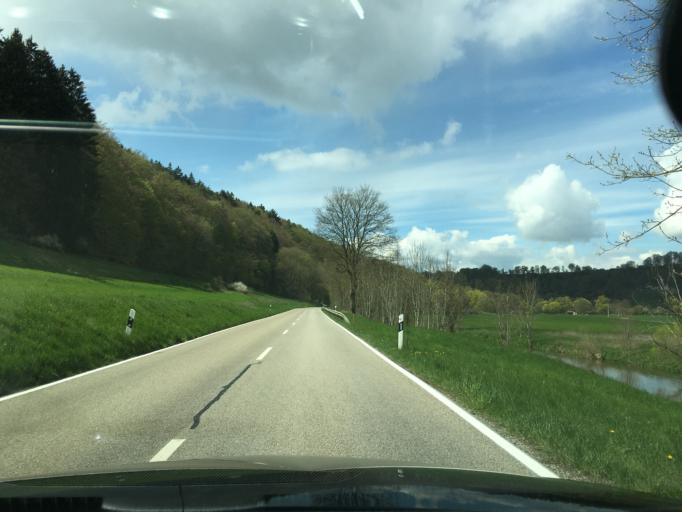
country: DE
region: Bavaria
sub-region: Upper Bavaria
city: Schernfeld
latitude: 48.8804
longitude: 11.0568
